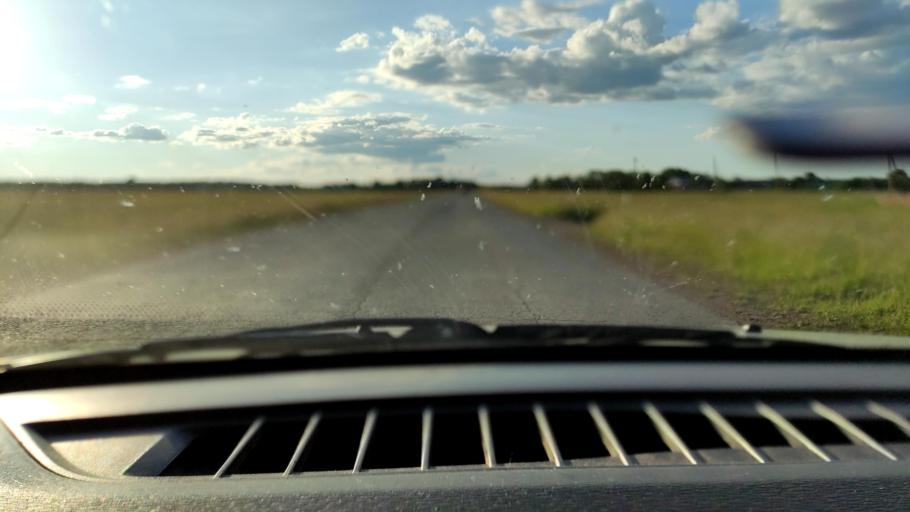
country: RU
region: Perm
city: Uinskoye
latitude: 57.0750
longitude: 56.5591
